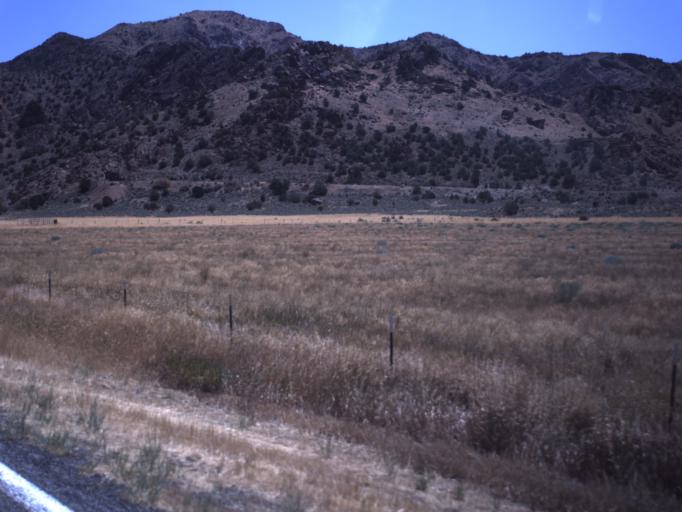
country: US
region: Utah
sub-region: Millard County
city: Delta
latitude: 39.5395
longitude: -112.2482
